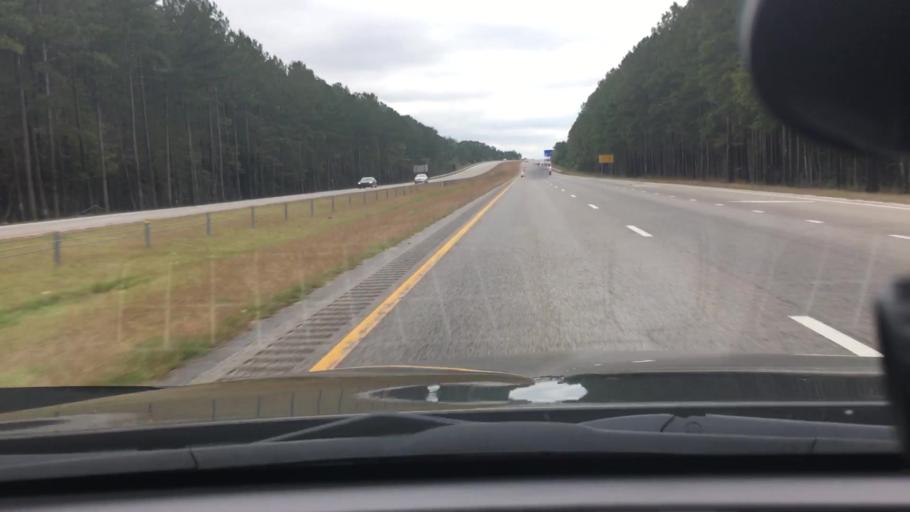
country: US
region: North Carolina
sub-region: Wilson County
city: Wilson
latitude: 35.6721
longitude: -77.8646
